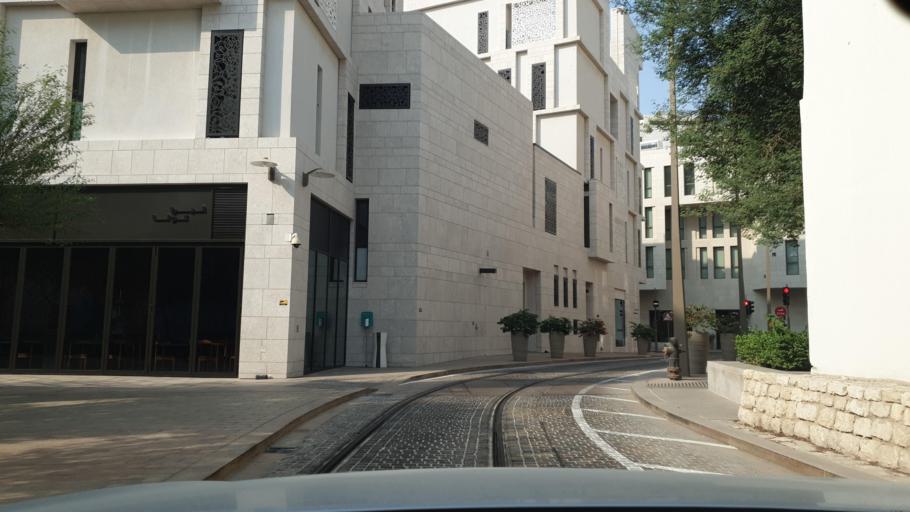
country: QA
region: Baladiyat ad Dawhah
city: Doha
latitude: 25.2872
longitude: 51.5262
